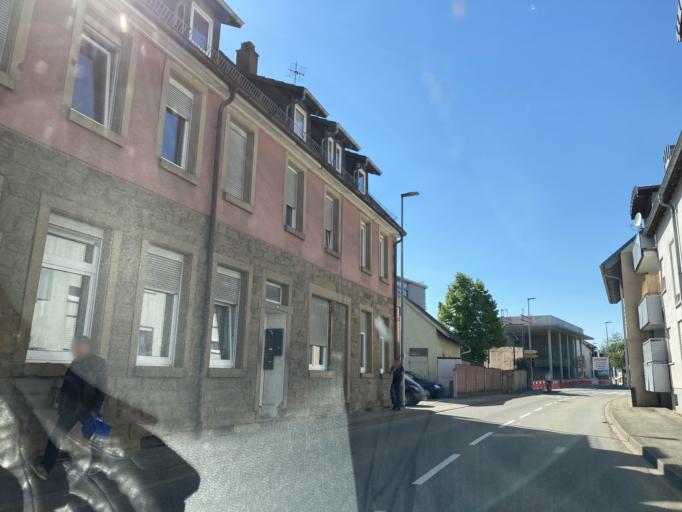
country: DE
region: Baden-Wuerttemberg
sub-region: Karlsruhe Region
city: Bretten
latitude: 49.0329
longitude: 8.7191
